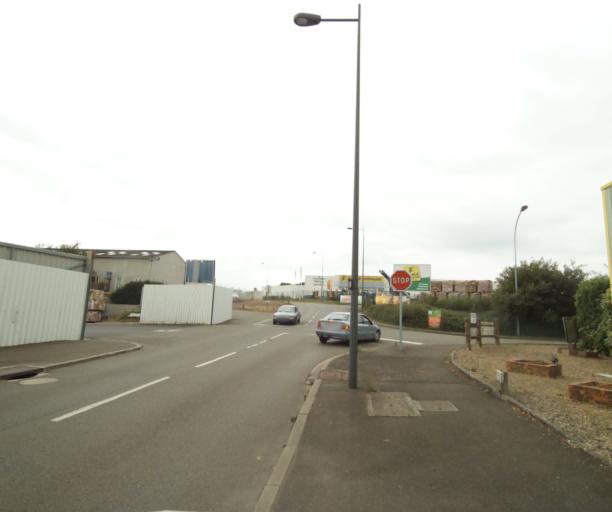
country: FR
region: Pays de la Loire
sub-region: Departement de la Sarthe
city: Solesmes
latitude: 47.8360
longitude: -0.3034
